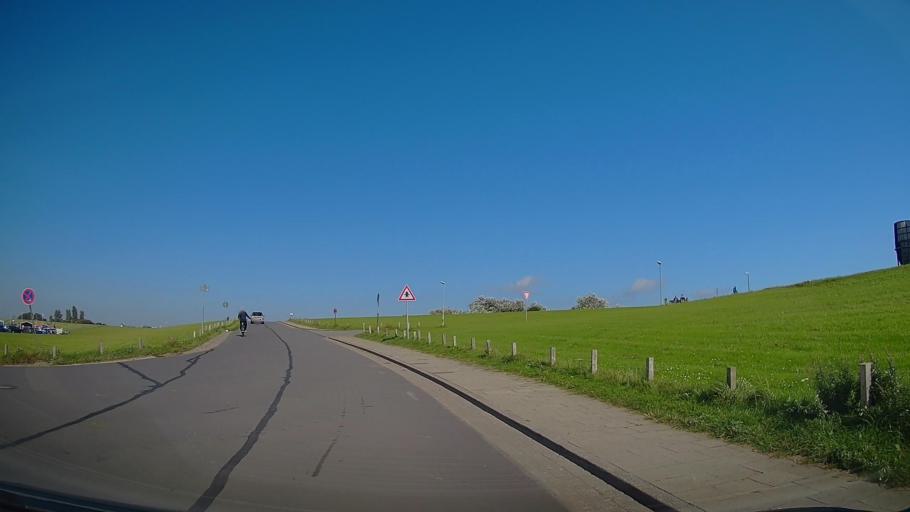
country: DE
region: Lower Saxony
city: Wremen
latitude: 53.6460
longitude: 8.4946
